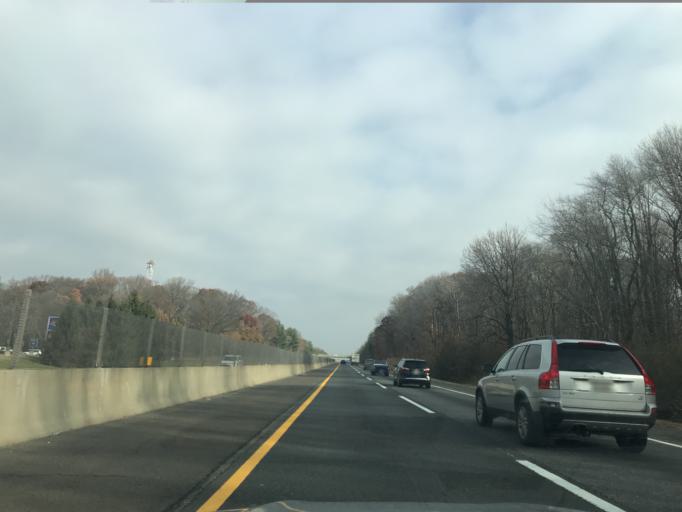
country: US
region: New Jersey
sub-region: Camden County
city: Ashland
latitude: 39.8842
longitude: -75.0026
